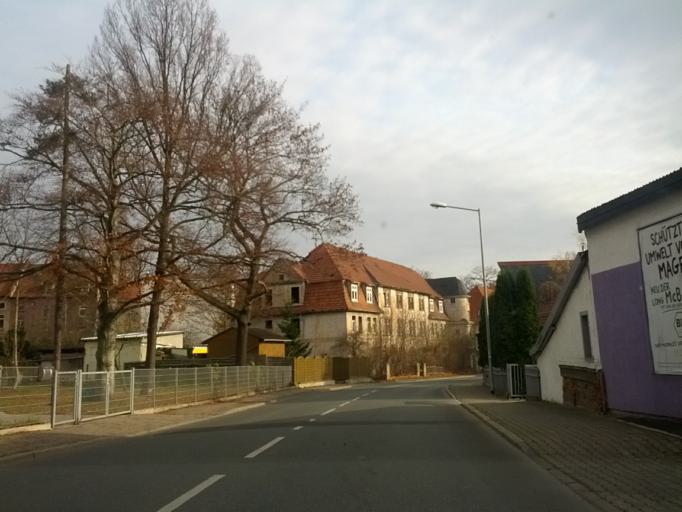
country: DE
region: Thuringia
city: Gotha
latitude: 50.9402
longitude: 10.6982
